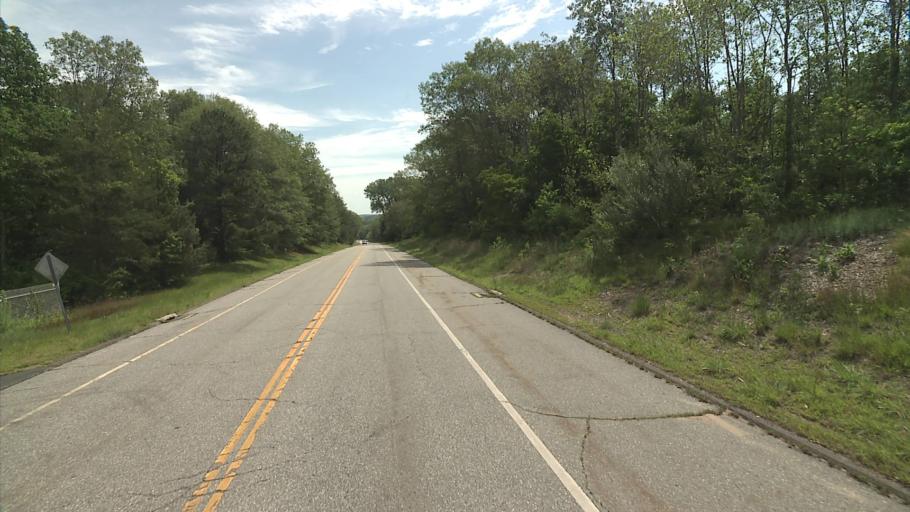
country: US
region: Connecticut
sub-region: Windham County
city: Willimantic
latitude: 41.7295
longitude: -72.2090
